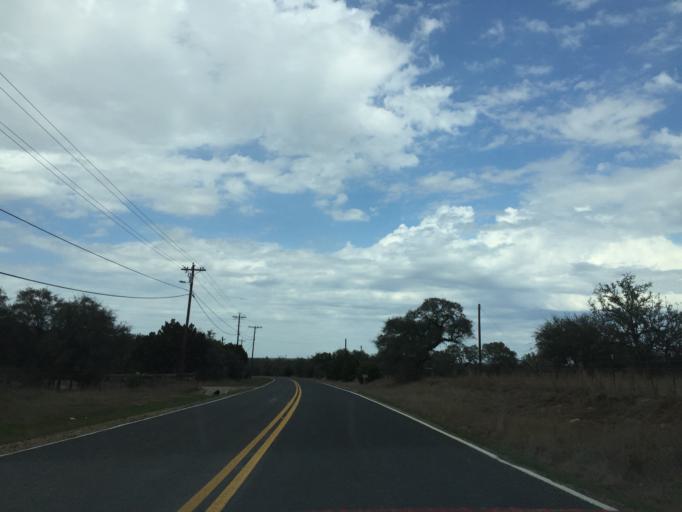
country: US
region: Texas
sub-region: Burnet County
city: Bertram
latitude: 30.7045
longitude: -97.9289
